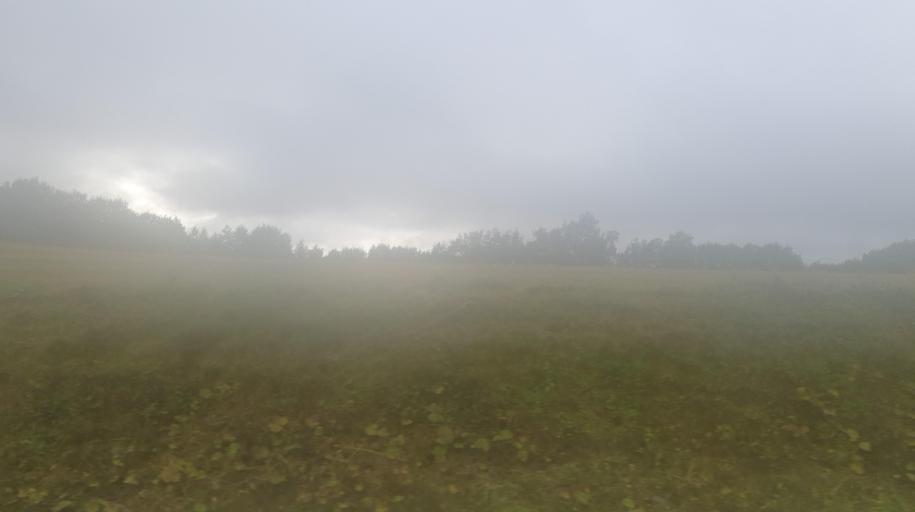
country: NO
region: Nord-Trondelag
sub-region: Levanger
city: Skogn
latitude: 63.6229
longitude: 11.1634
